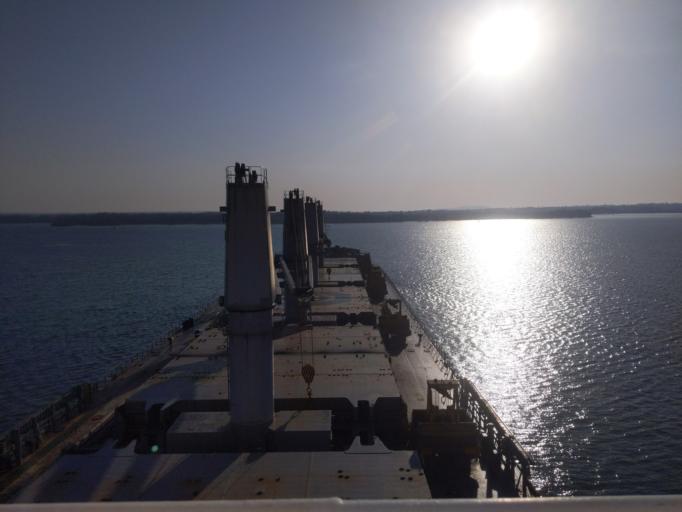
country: ZA
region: KwaZulu-Natal
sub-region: uThungulu District Municipality
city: Richards Bay
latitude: -28.8037
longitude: 32.0533
